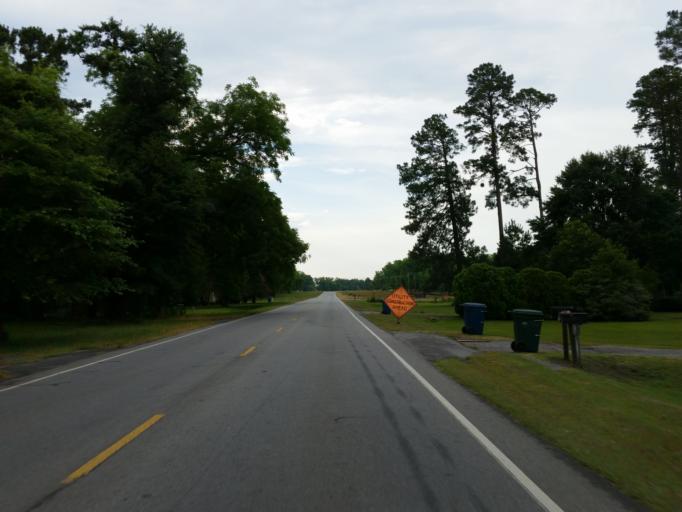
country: US
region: Georgia
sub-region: Dooly County
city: Vienna
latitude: 32.0406
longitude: -83.7944
